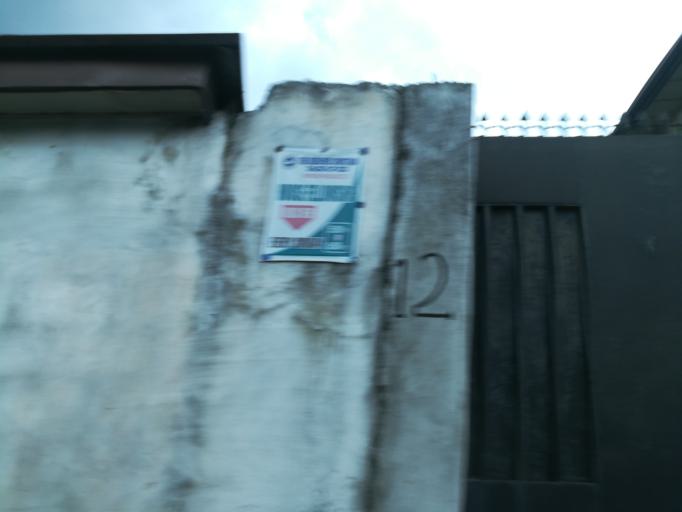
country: NG
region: Rivers
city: Port Harcourt
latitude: 4.8153
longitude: 7.0695
